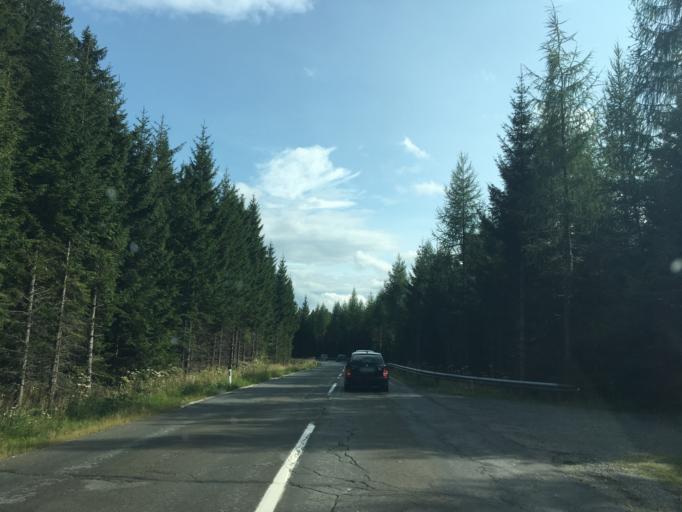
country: AT
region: Styria
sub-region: Politischer Bezirk Deutschlandsberg
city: Kloster
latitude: 46.8328
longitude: 15.0352
